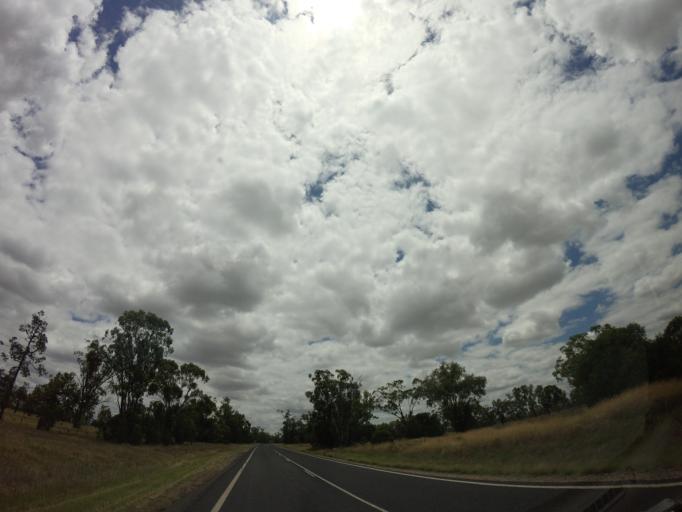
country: AU
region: Queensland
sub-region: Goondiwindi
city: Goondiwindi
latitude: -28.4951
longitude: 150.2922
